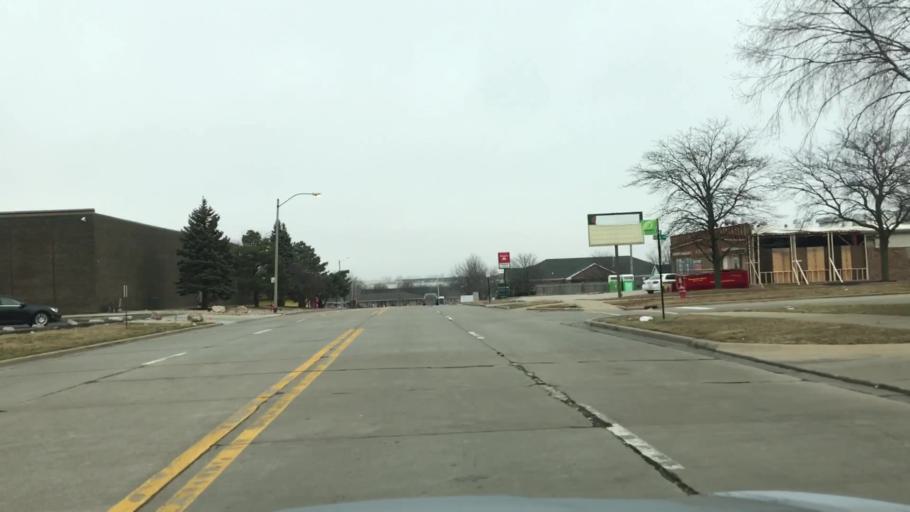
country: US
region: Illinois
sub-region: McLean County
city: Normal
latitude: 40.5111
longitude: -88.9554
